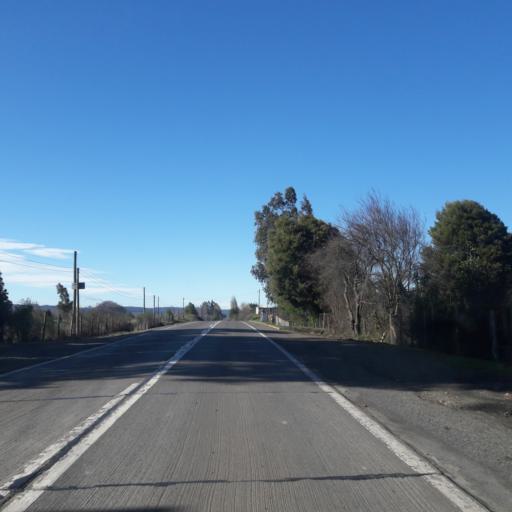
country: CL
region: Araucania
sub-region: Provincia de Malleco
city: Angol
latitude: -37.7666
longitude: -72.5594
